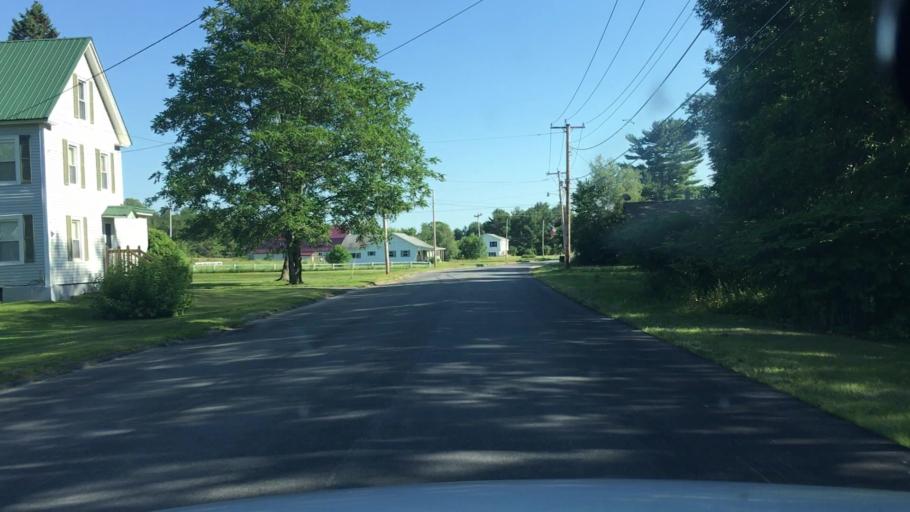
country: US
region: Maine
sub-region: Penobscot County
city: Howland
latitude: 45.2350
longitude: -68.6490
